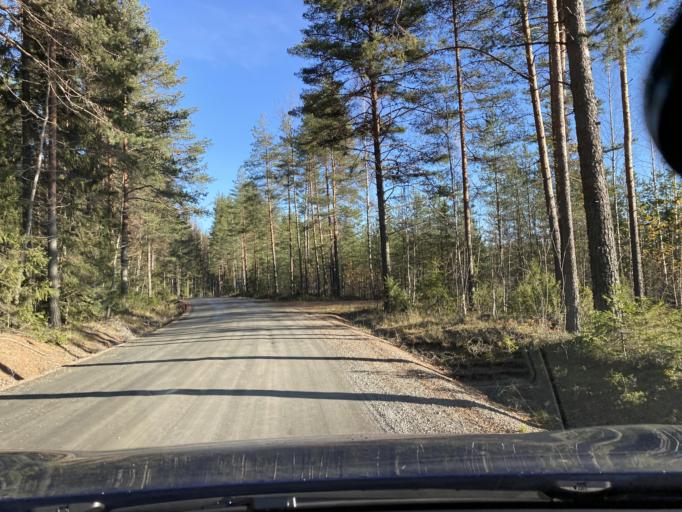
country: FI
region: Haeme
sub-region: Haemeenlinna
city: Kalvola
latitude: 61.0090
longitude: 24.1252
